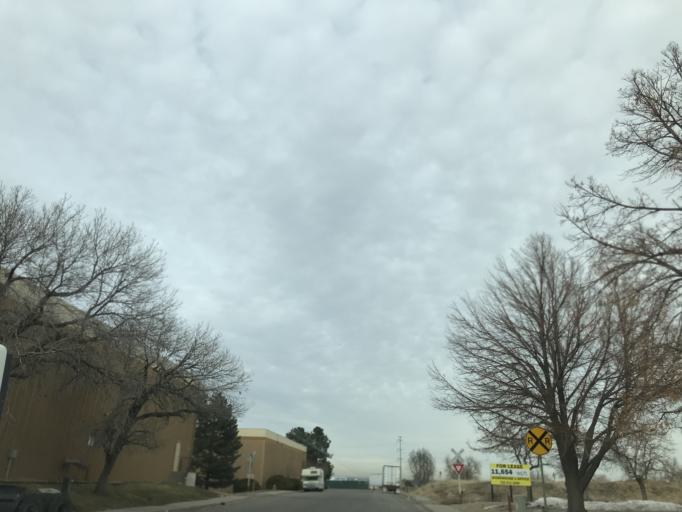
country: US
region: Colorado
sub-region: Adams County
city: Commerce City
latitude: 39.7813
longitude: -104.9159
